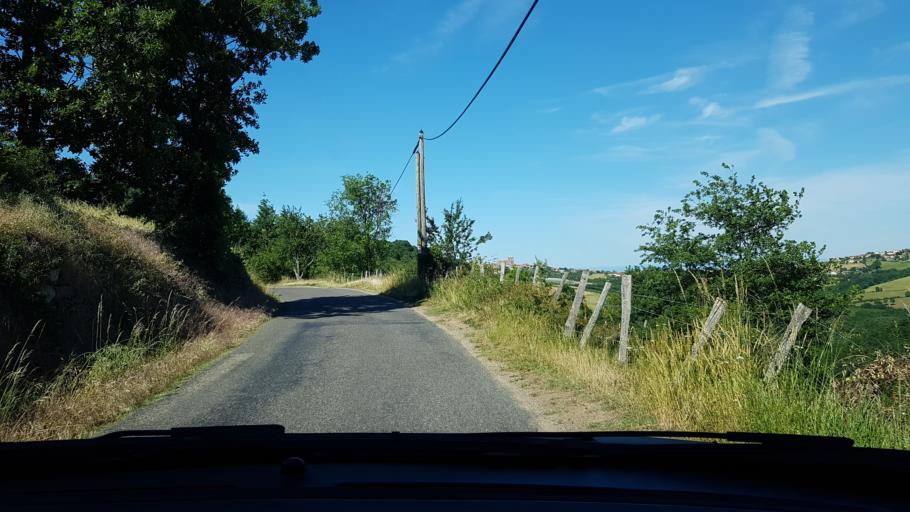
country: FR
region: Rhone-Alpes
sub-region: Departement du Rhone
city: Saint-Didier-sous-Riverie
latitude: 45.5857
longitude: 4.5904
